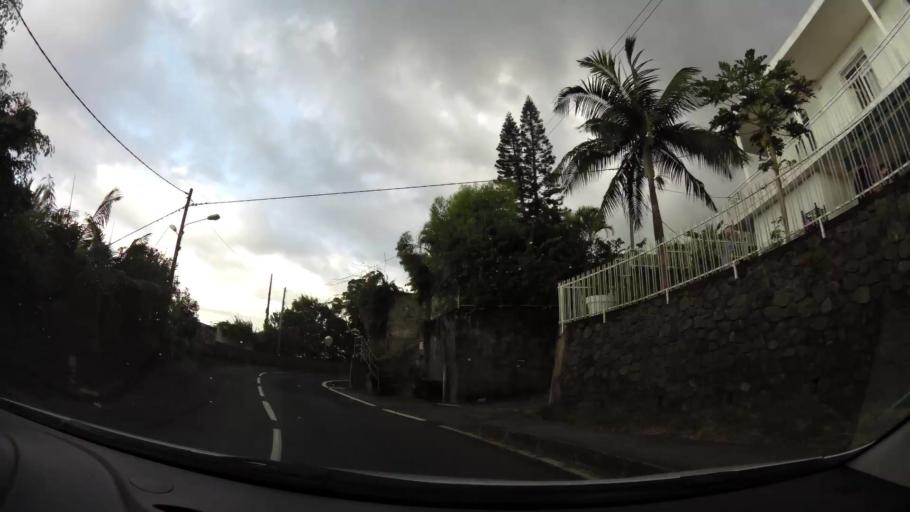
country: RE
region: Reunion
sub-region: Reunion
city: Saint-Denis
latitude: -20.9009
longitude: 55.4435
